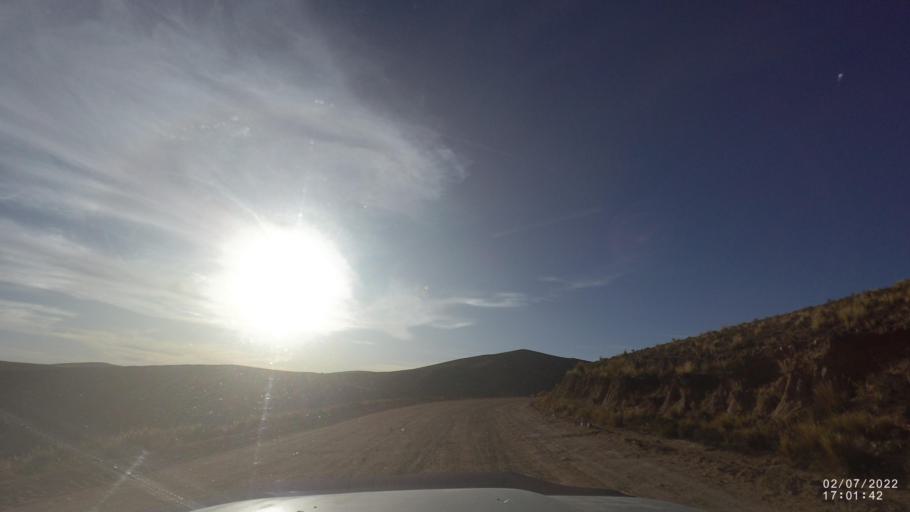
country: BO
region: Cochabamba
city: Irpa Irpa
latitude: -17.9312
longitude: -66.5537
